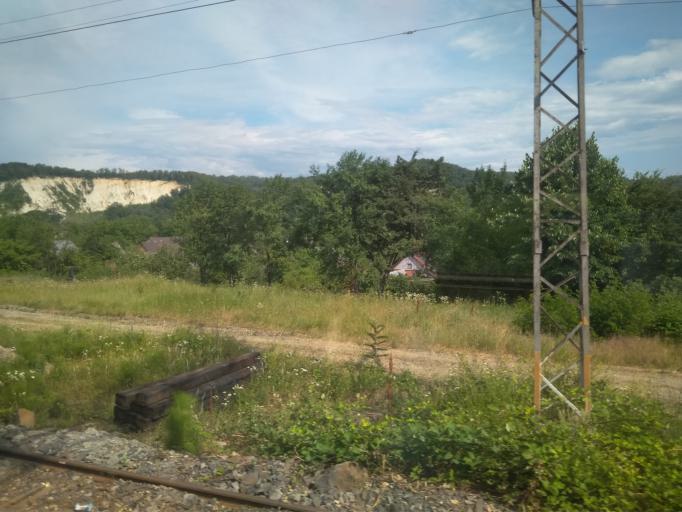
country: RU
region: Krasnodarskiy
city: Khadyzhensk
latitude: 44.4388
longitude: 39.4814
